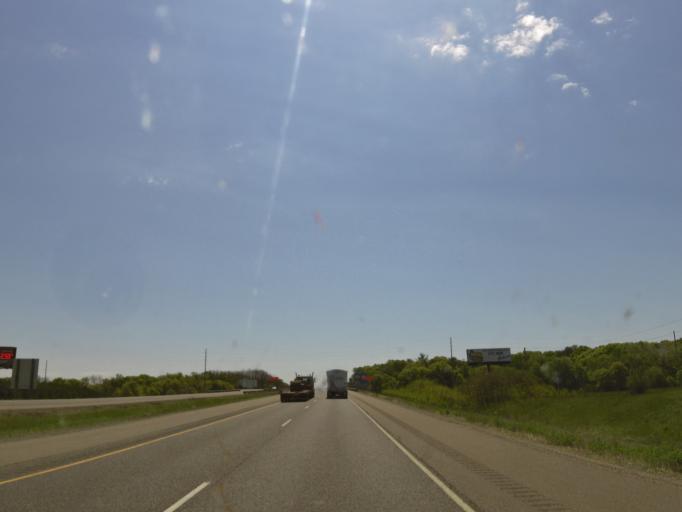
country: US
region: Wisconsin
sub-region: Jackson County
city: Black River Falls
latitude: 44.3020
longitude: -90.8310
